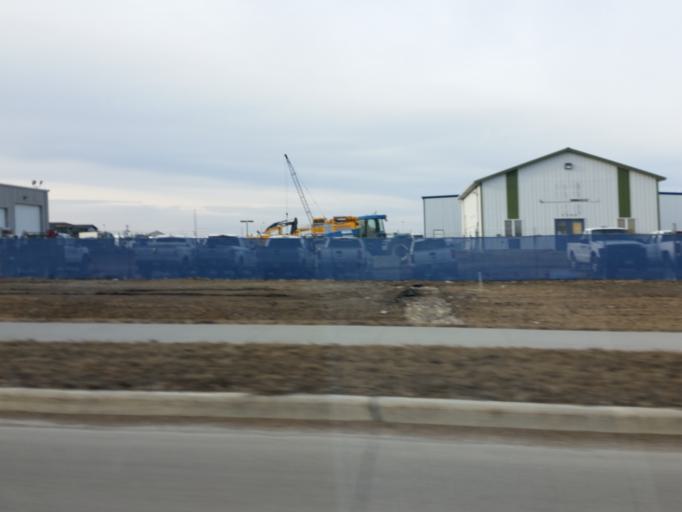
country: US
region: North Dakota
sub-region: Cass County
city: West Fargo
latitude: 46.8772
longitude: -96.9331
